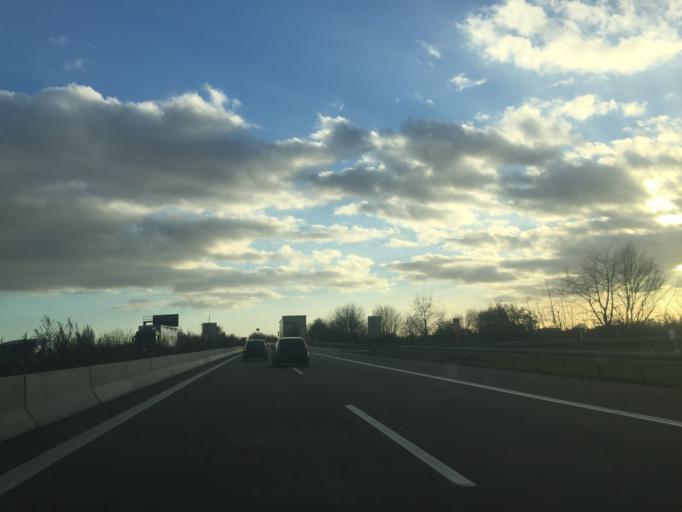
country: DE
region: Baden-Wuerttemberg
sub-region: Karlsruhe Region
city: Dossenheim
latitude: 49.4483
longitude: 8.6461
